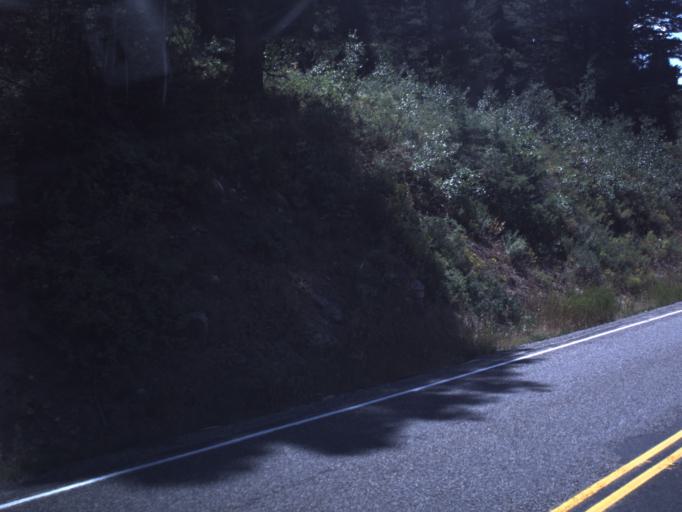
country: US
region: Utah
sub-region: Cache County
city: Richmond
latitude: 41.9394
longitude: -111.5534
